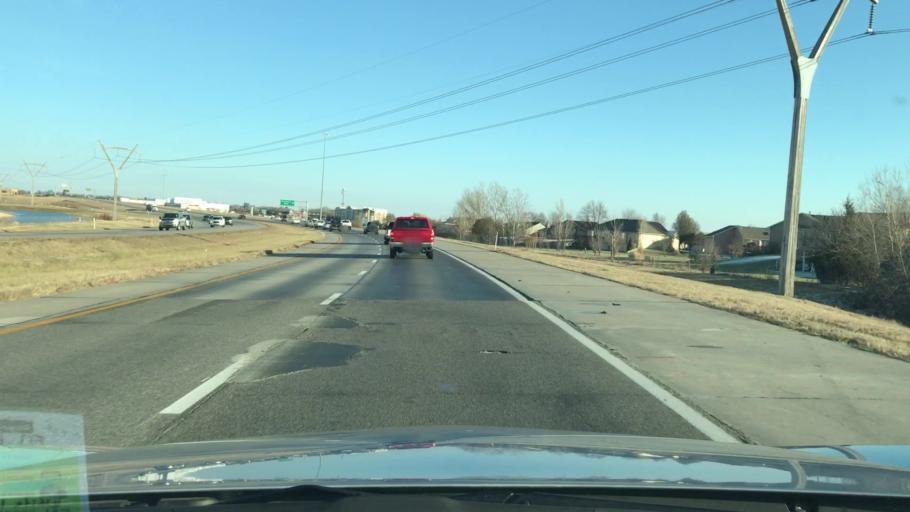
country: US
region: Kansas
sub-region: Sedgwick County
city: Bellaire
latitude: 37.7307
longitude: -97.2171
